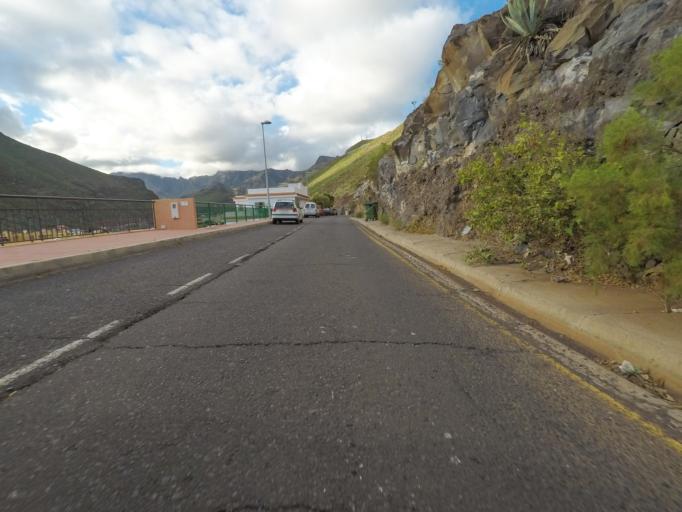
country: ES
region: Canary Islands
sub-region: Provincia de Santa Cruz de Tenerife
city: San Sebastian de la Gomera
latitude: 28.0957
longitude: -17.1132
